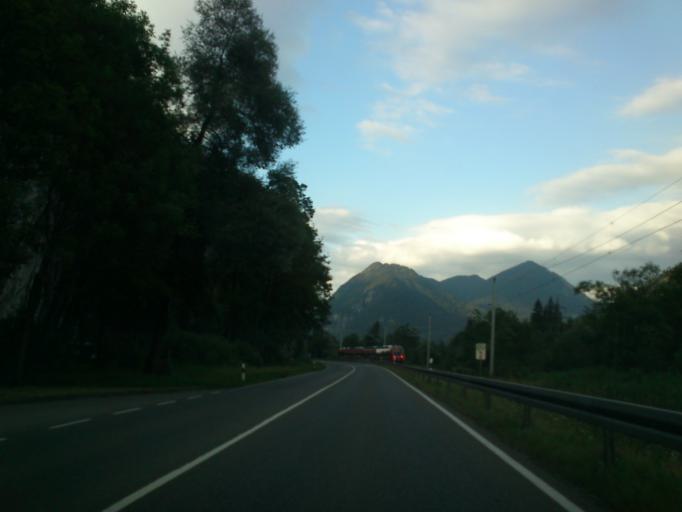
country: DE
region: Bavaria
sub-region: Upper Bavaria
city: Oberau
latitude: 47.5752
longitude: 11.1609
